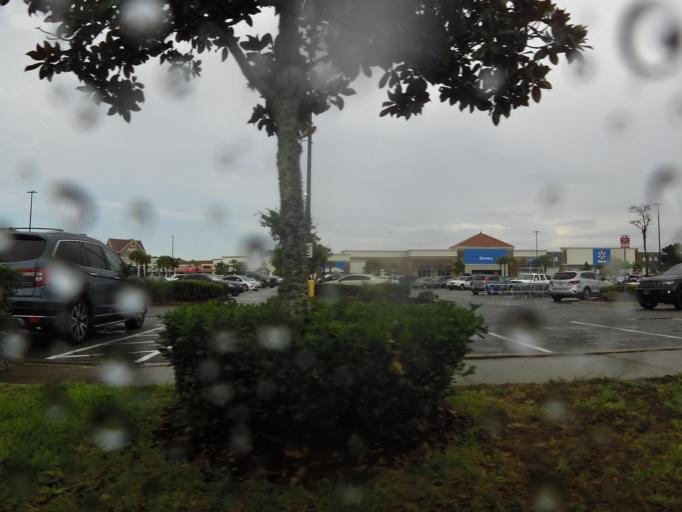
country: US
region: Florida
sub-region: Duval County
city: Jacksonville
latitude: 30.4788
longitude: -81.6403
